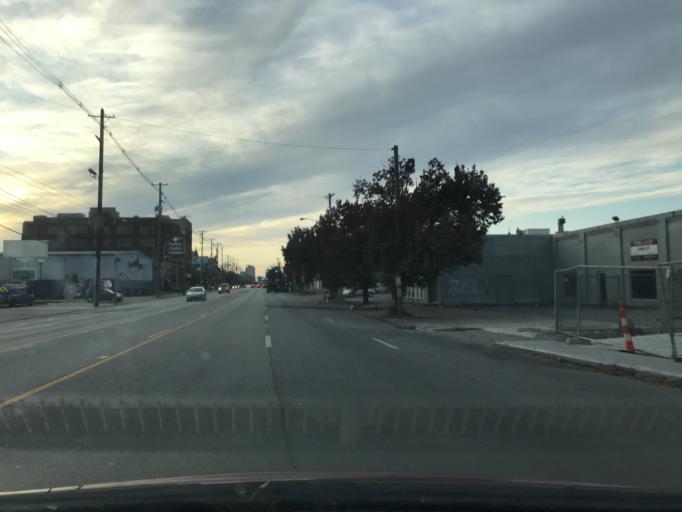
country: US
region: Kentucky
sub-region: Jefferson County
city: Louisville
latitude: 38.2444
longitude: -85.7357
